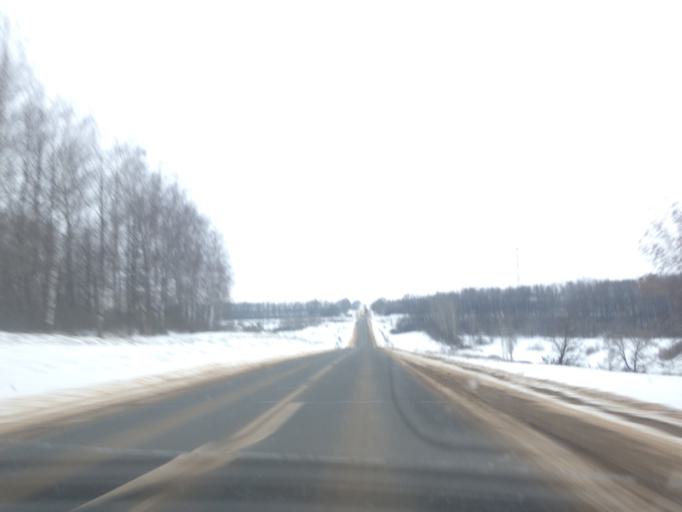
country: RU
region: Tula
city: Shchekino
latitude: 53.9598
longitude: 37.4936
